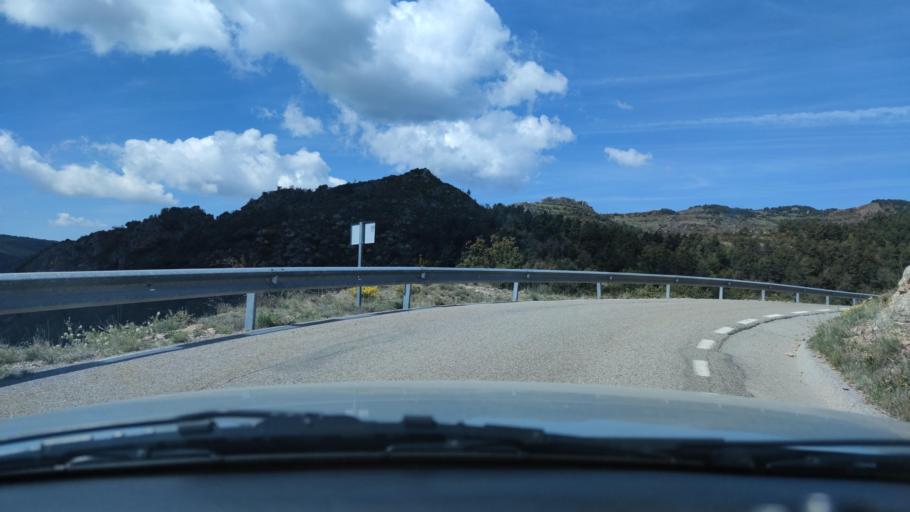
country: ES
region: Catalonia
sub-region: Provincia de Lleida
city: Coll de Nargo
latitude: 42.2891
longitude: 1.2536
